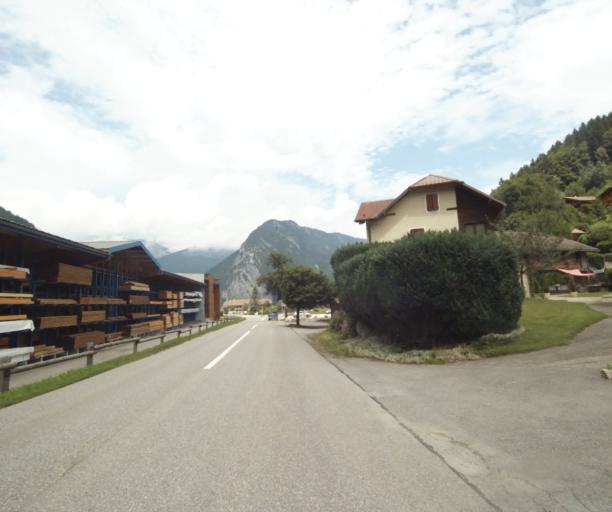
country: FR
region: Rhone-Alpes
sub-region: Departement de la Haute-Savoie
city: Thones
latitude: 45.8685
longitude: 6.3243
